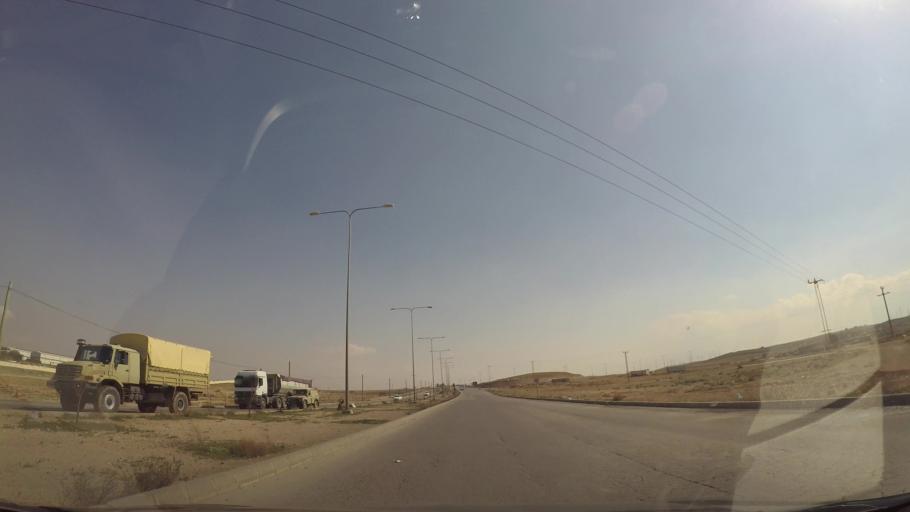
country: JO
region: Zarqa
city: Zarqa
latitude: 32.0571
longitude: 36.1292
